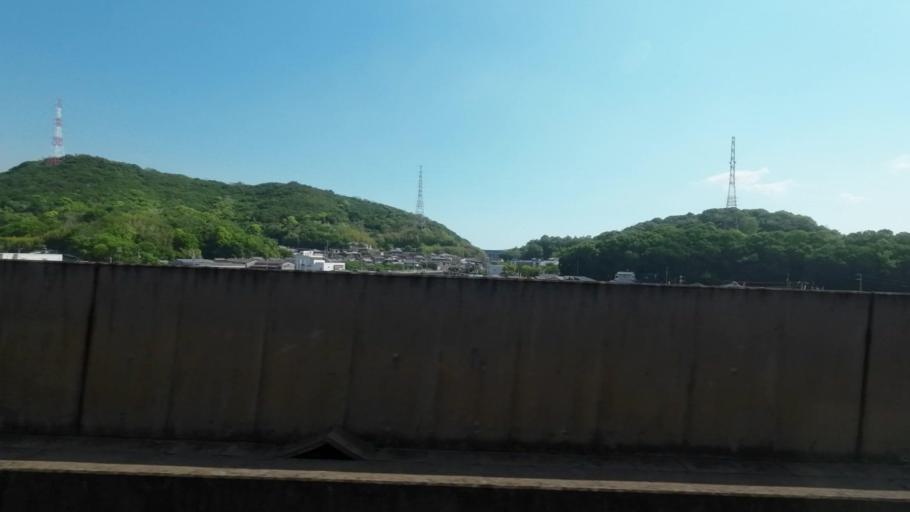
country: JP
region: Kagawa
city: Sakaidecho
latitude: 34.3105
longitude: 133.8338
